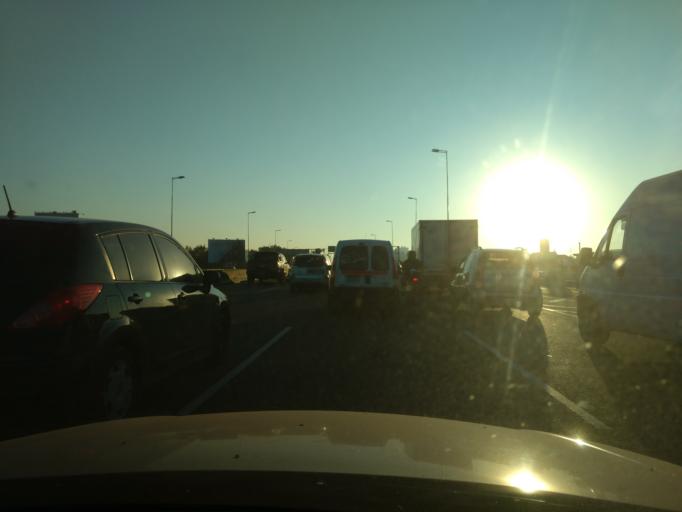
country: AR
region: Buenos Aires F.D.
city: Villa Santa Rita
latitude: -34.6410
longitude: -58.4592
